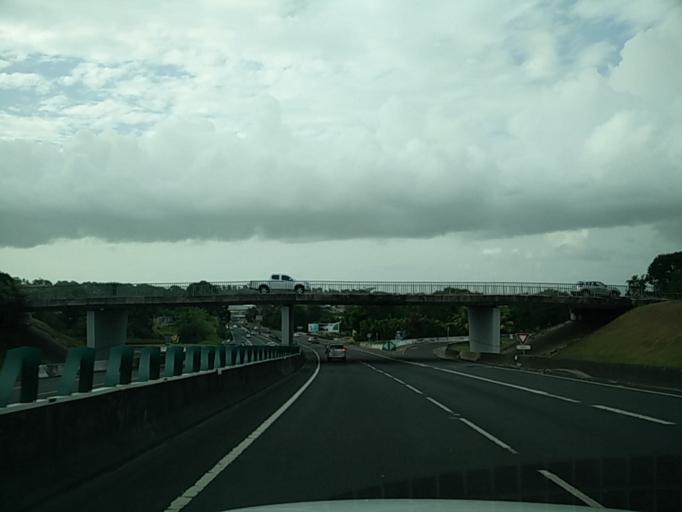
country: GP
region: Guadeloupe
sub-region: Guadeloupe
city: Petit-Bourg
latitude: 16.1964
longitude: -61.6058
